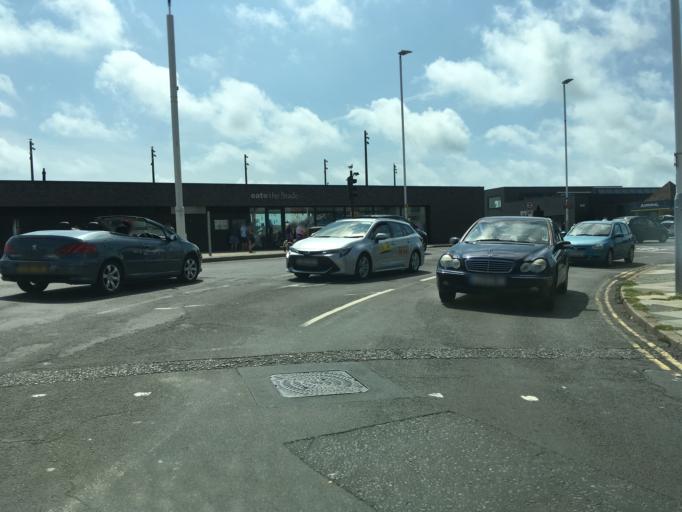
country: GB
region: England
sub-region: East Sussex
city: Hastings
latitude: 50.8564
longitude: 0.5921
